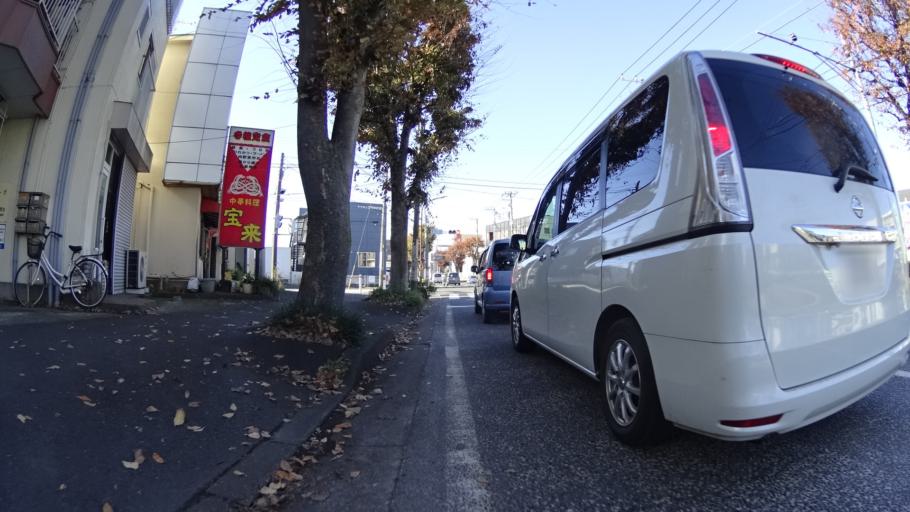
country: JP
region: Kanagawa
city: Zama
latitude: 35.5702
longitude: 139.3591
